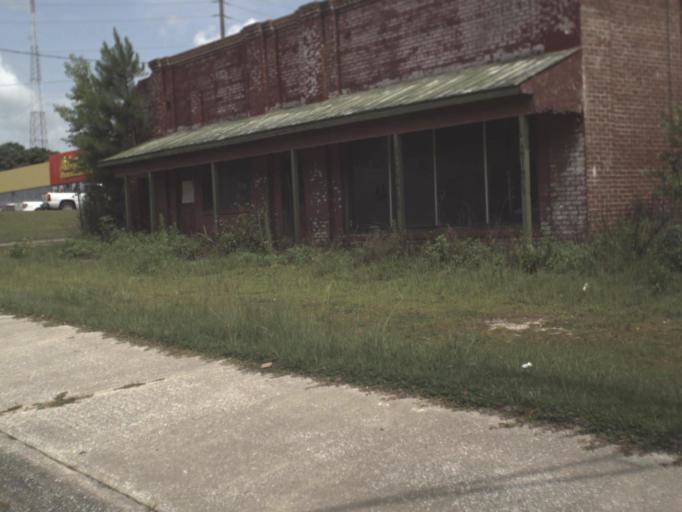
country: US
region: Florida
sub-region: Madison County
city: Madison
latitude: 30.4694
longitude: -83.4074
